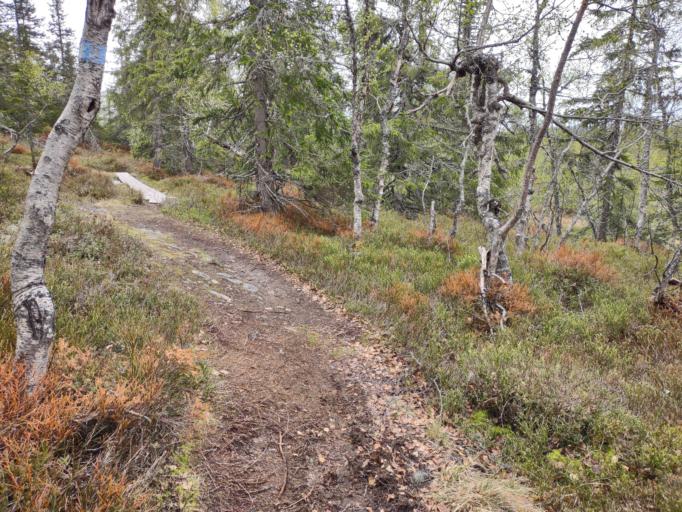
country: NO
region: Oppland
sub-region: Gran
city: Jaren
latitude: 60.4276
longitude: 10.6862
